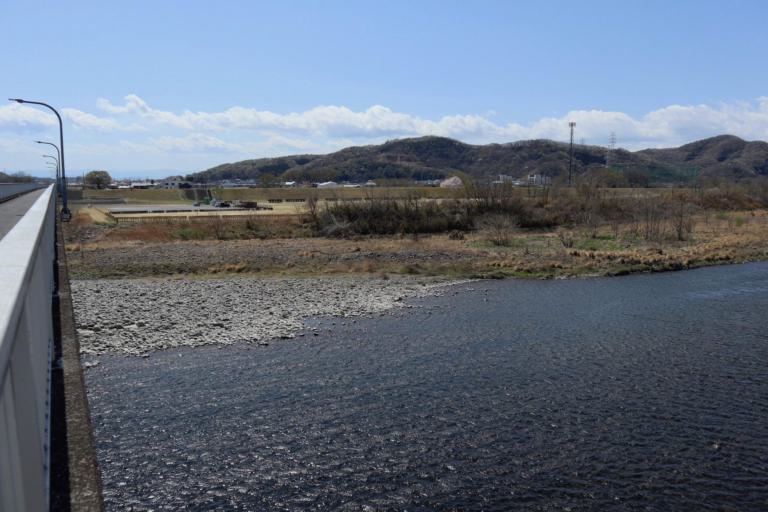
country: JP
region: Gunma
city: Ota
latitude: 36.3573
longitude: 139.3865
